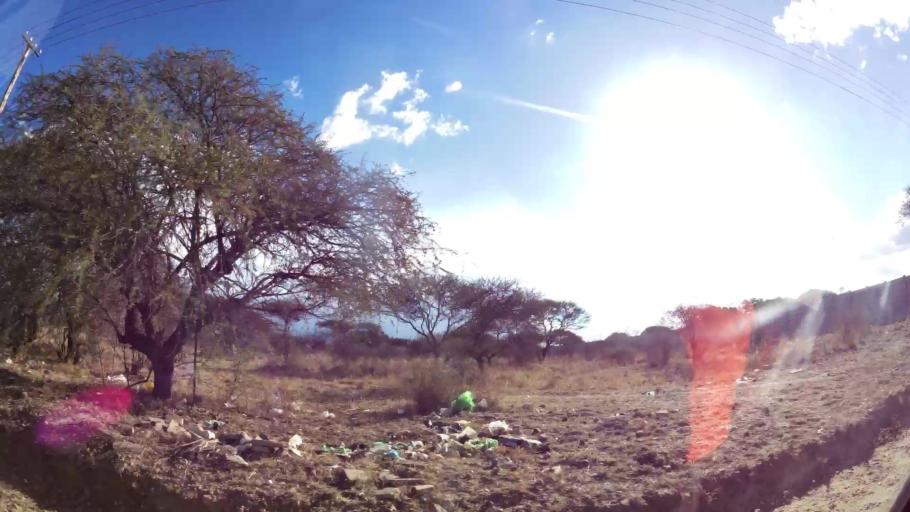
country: ZA
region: Limpopo
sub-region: Capricorn District Municipality
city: Polokwane
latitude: -23.9361
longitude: 29.4444
